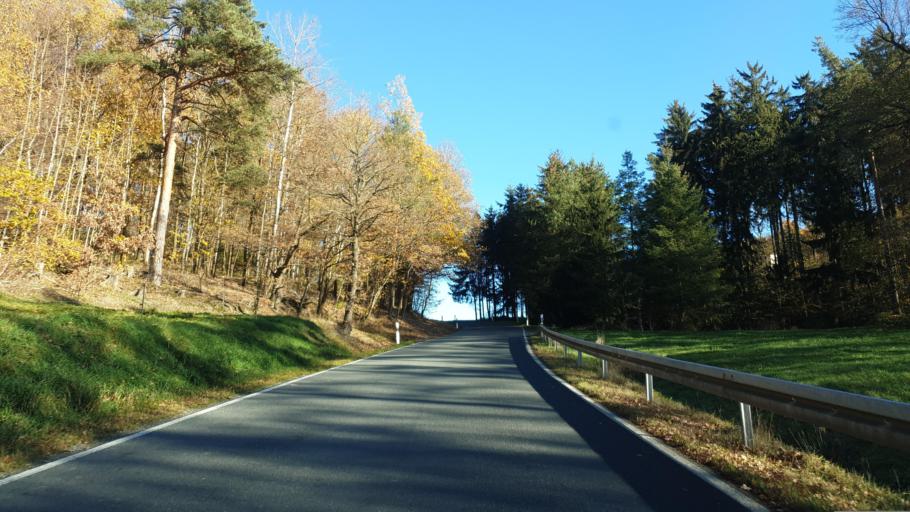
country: DE
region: Saxony
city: Elsterberg
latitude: 50.6306
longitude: 12.1474
